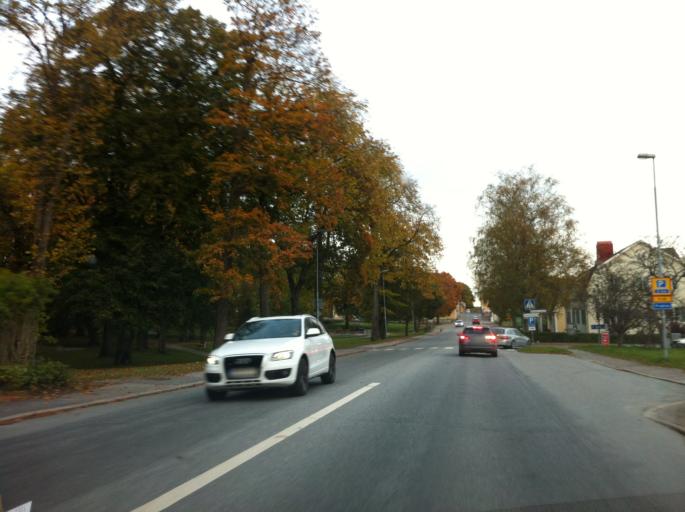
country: SE
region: OErebro
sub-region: Nora Kommun
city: Nora
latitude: 59.5060
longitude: 15.0253
